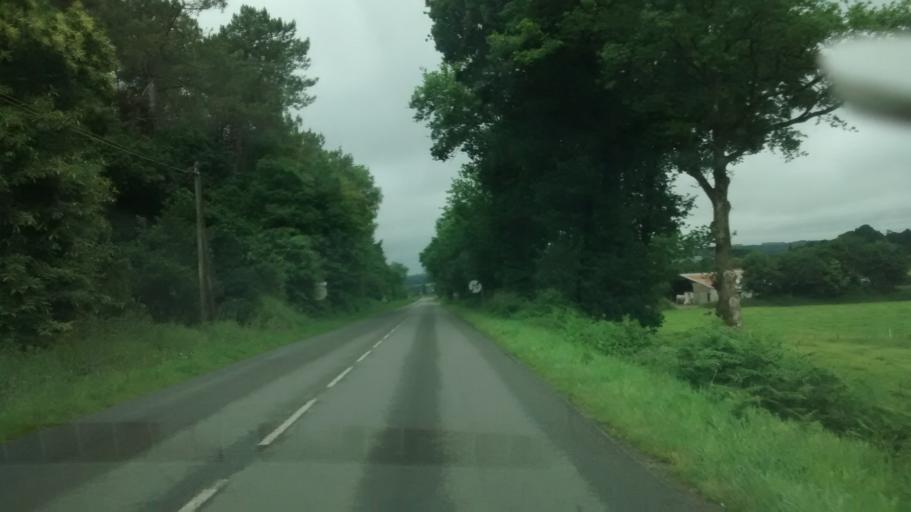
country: FR
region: Brittany
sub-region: Departement du Morbihan
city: Serent
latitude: 47.8193
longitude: -2.4857
